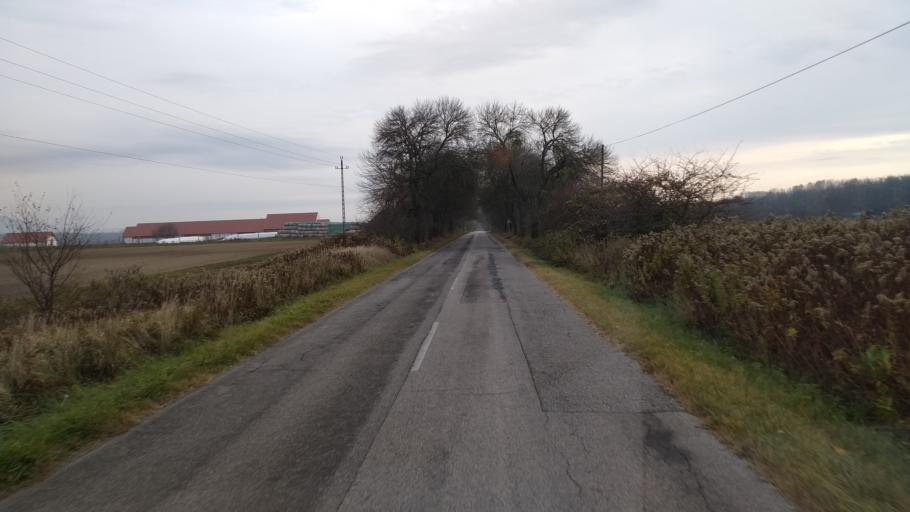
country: HU
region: Pest
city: Dunabogdany
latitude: 47.8004
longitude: 19.0422
